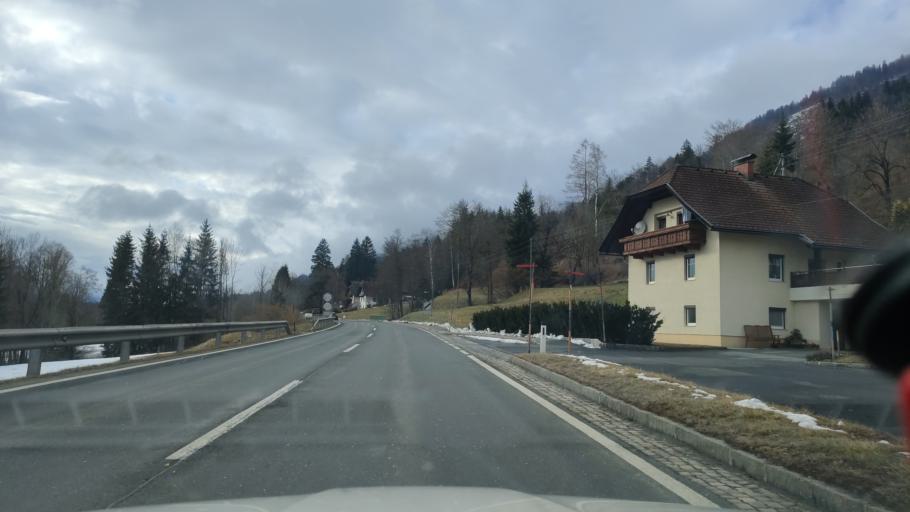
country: AT
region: Carinthia
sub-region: Politischer Bezirk Hermagor
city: Hermagor
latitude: 46.6188
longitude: 13.3323
